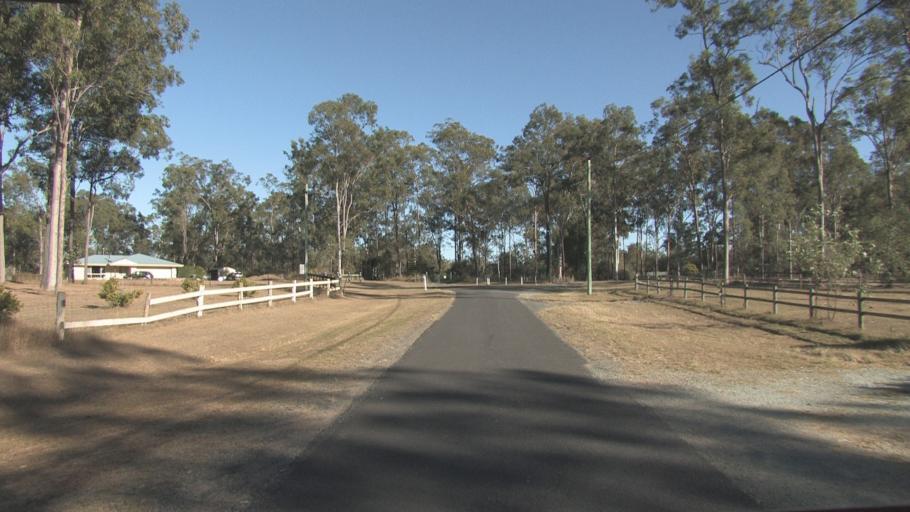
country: AU
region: Queensland
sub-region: Logan
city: North Maclean
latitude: -27.7930
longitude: 152.9764
